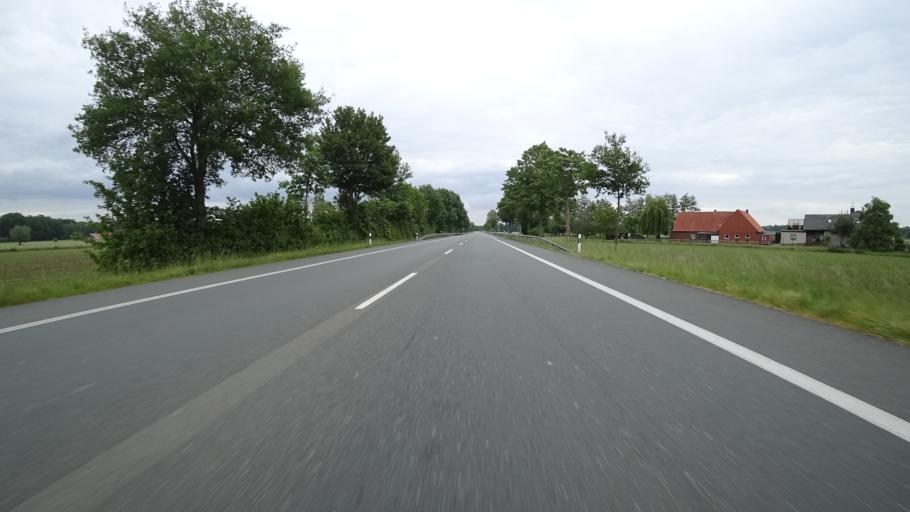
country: DE
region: North Rhine-Westphalia
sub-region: Regierungsbezirk Detmold
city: Delbruck
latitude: 51.7779
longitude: 8.5080
